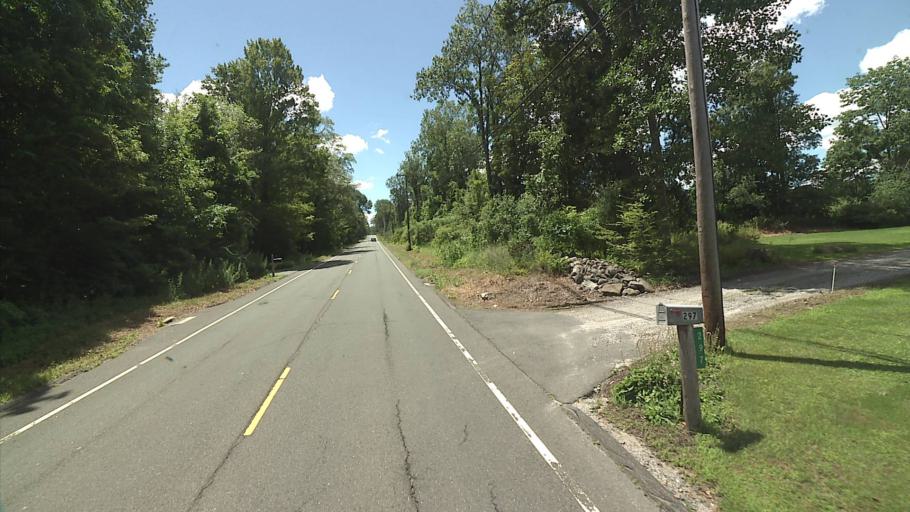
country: US
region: Connecticut
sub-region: Litchfield County
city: New Hartford Center
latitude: 41.8706
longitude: -72.9977
